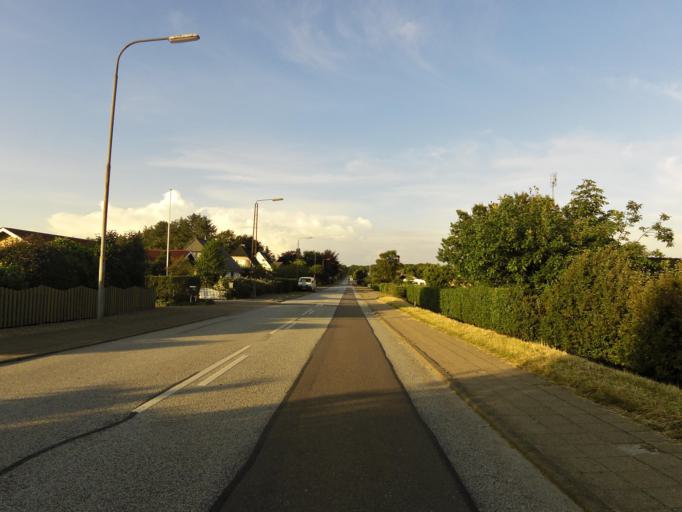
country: DK
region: South Denmark
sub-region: Tonder Kommune
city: Sherrebek
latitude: 55.1629
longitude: 8.7667
